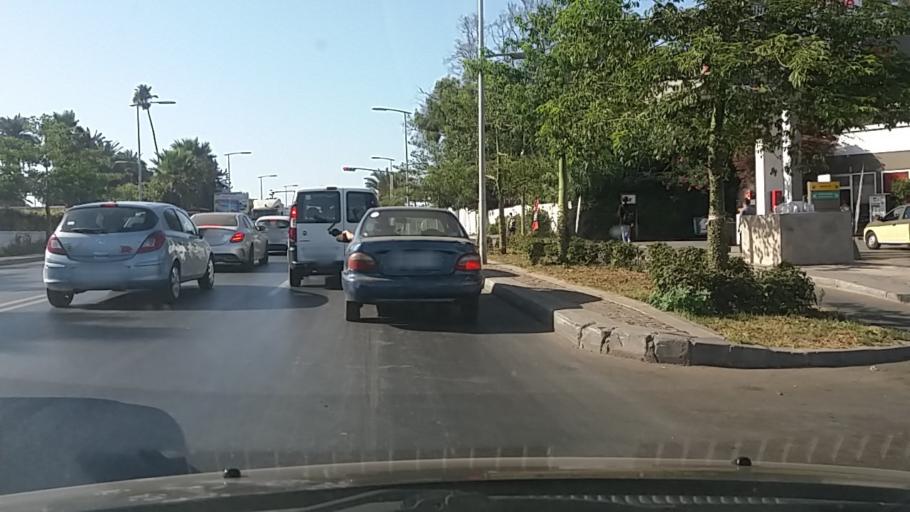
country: MA
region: Rabat-Sale-Zemmour-Zaer
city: Sale
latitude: 34.0429
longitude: -6.8172
